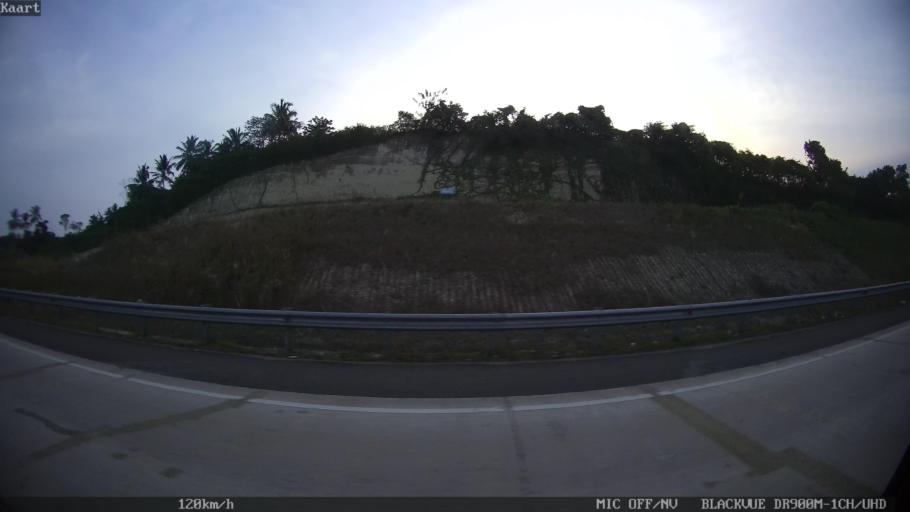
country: ID
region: Lampung
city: Penengahan
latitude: -5.7983
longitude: 105.7288
